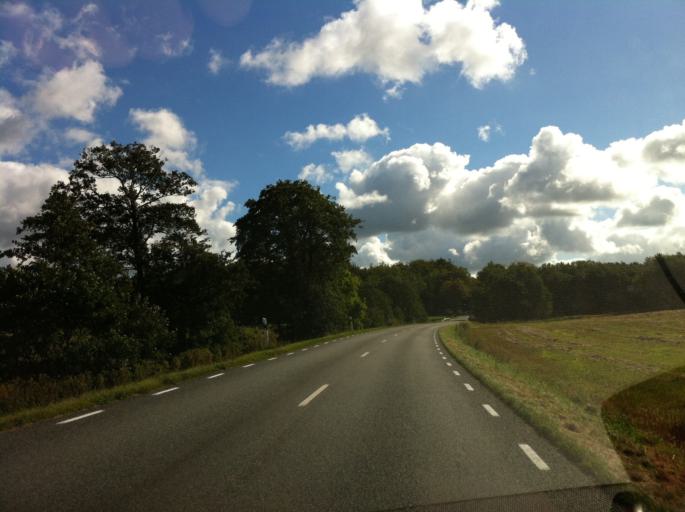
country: SE
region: Skane
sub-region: Kristianstads Kommun
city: Degeberga
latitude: 55.7852
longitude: 13.8723
